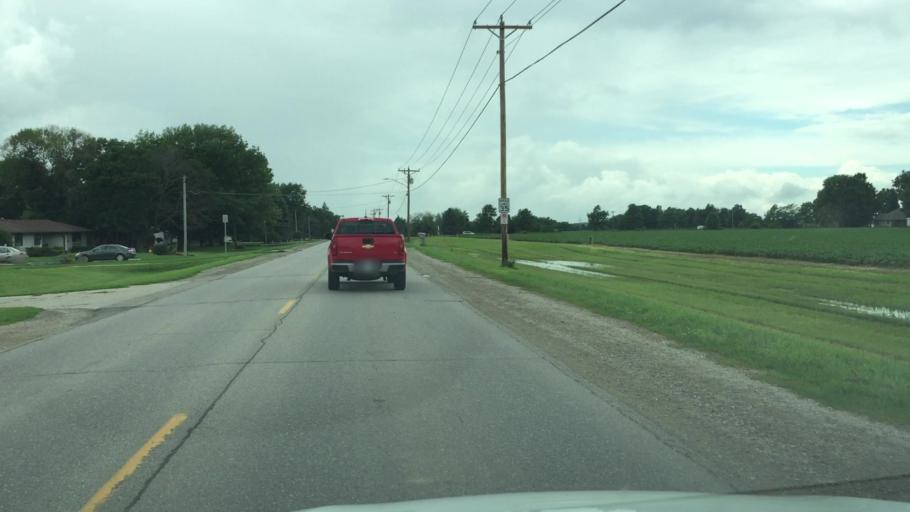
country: US
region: Iowa
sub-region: Jasper County
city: Newton
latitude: 41.7172
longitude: -93.0537
